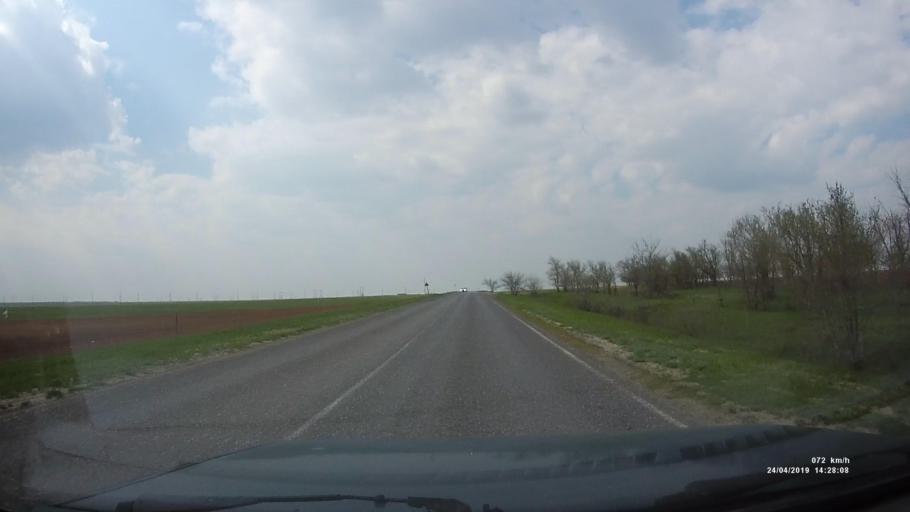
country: RU
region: Kalmykiya
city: Arshan'
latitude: 46.3364
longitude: 44.0333
